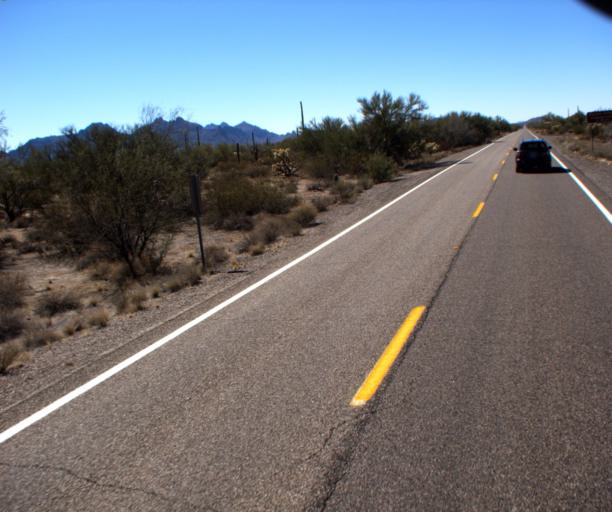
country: US
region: Arizona
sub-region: Pima County
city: Ajo
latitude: 32.1687
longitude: -112.7631
